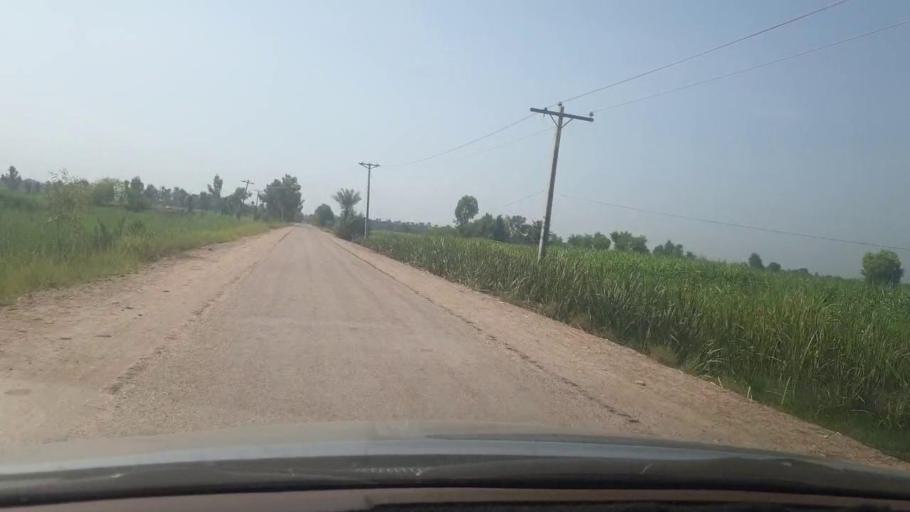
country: PK
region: Sindh
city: Ranipur
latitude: 27.2918
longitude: 68.5750
